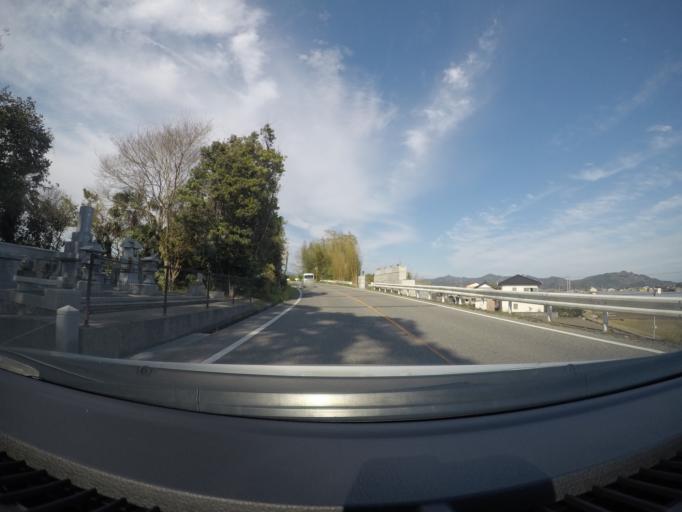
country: JP
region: Kochi
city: Kochi-shi
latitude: 33.5887
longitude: 133.6664
